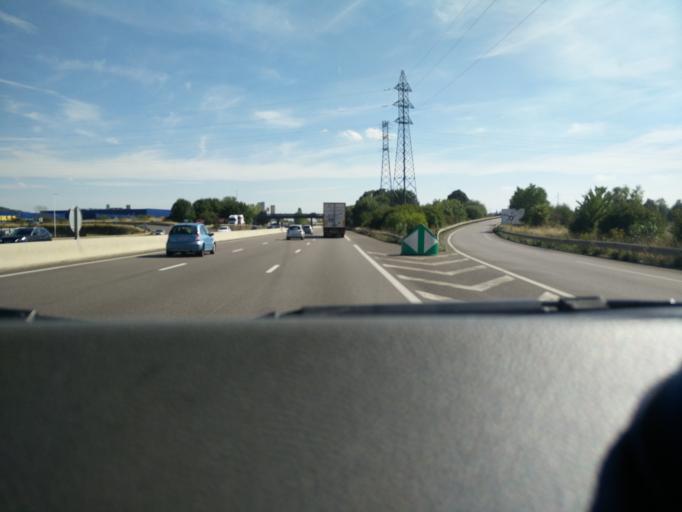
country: FR
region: Lorraine
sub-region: Departement de la Moselle
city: Saint-Julien-les-Metz
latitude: 49.1533
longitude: 6.1831
